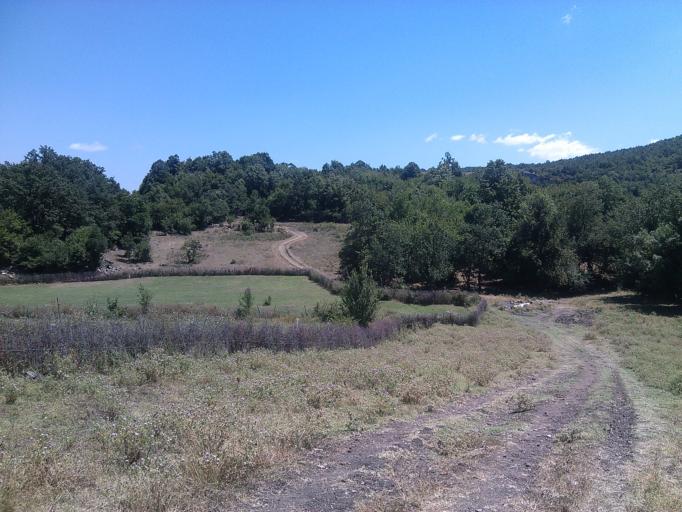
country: BG
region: Kurdzhali
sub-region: Obshtina Kurdzhali
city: Kurdzhali
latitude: 41.5883
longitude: 25.4195
